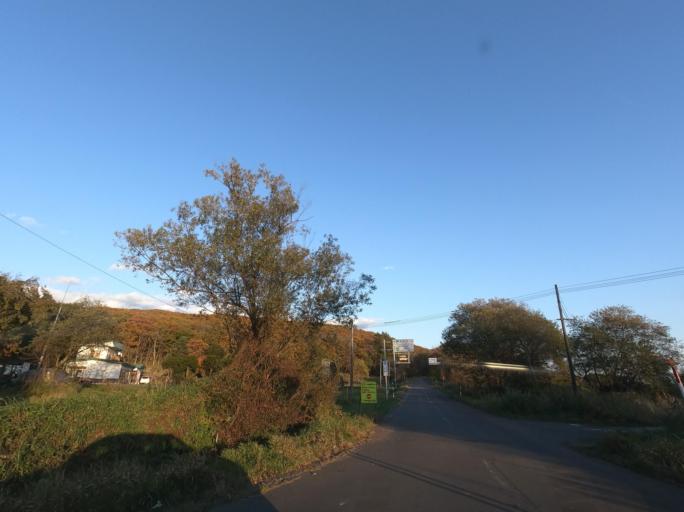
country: JP
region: Hokkaido
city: Kushiro
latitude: 43.2262
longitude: 144.4356
